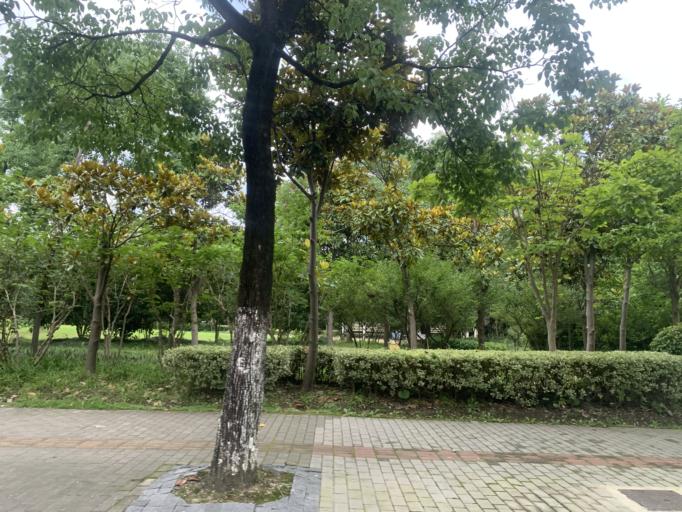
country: CN
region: Shanghai Shi
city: Huamu
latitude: 31.2054
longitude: 121.5314
